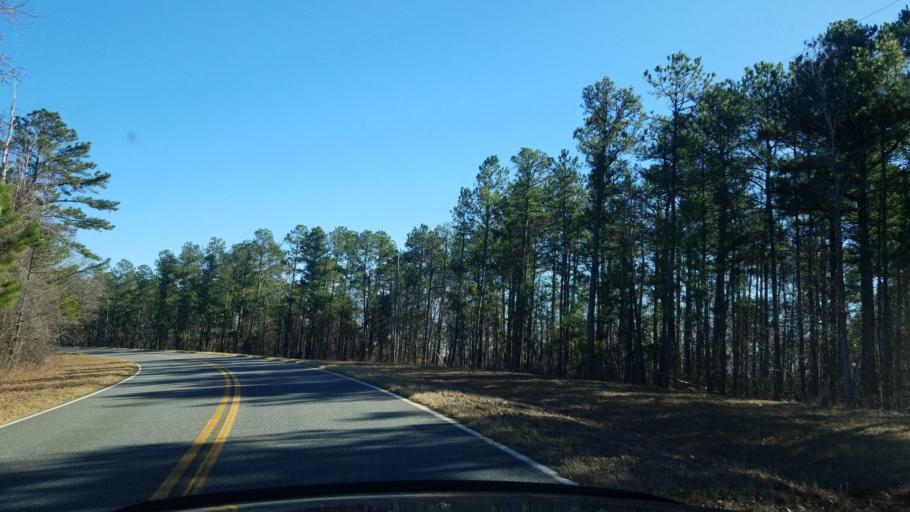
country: US
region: Georgia
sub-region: Meriwether County
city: Manchester
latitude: 32.8425
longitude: -84.6742
